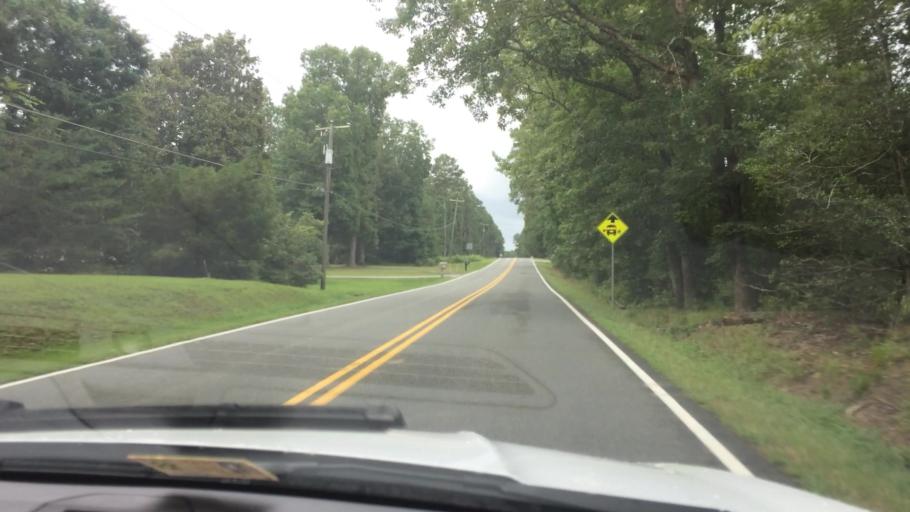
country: US
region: Virginia
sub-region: New Kent County
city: New Kent
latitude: 37.4713
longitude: -77.0328
